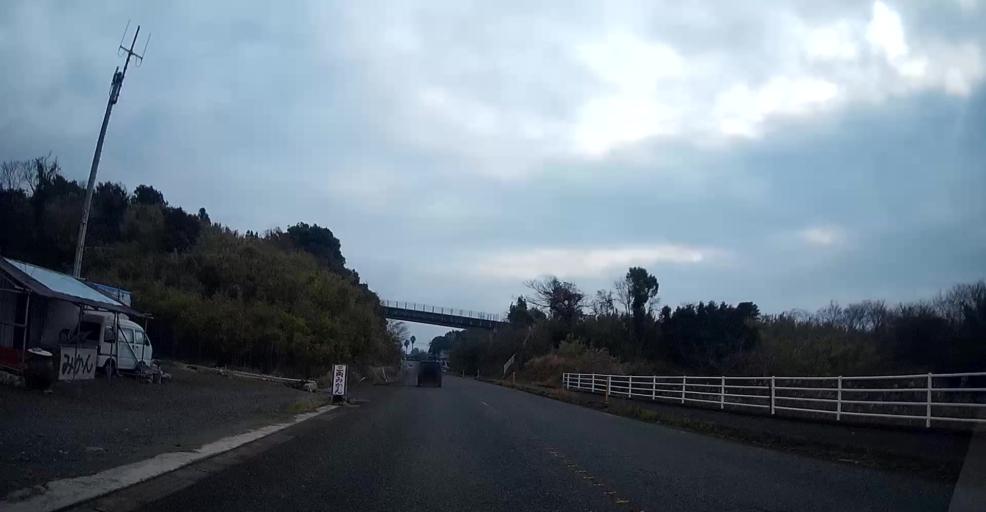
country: JP
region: Kumamoto
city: Matsubase
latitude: 32.6254
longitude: 130.5361
